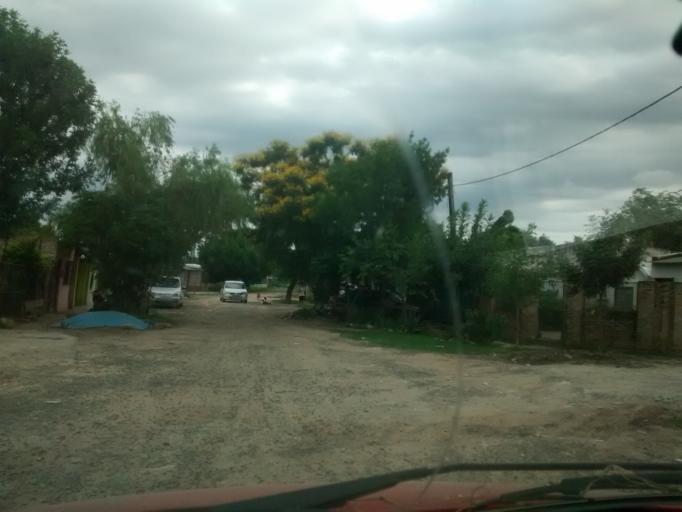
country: AR
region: Chaco
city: Resistencia
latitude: -27.4241
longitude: -58.9741
